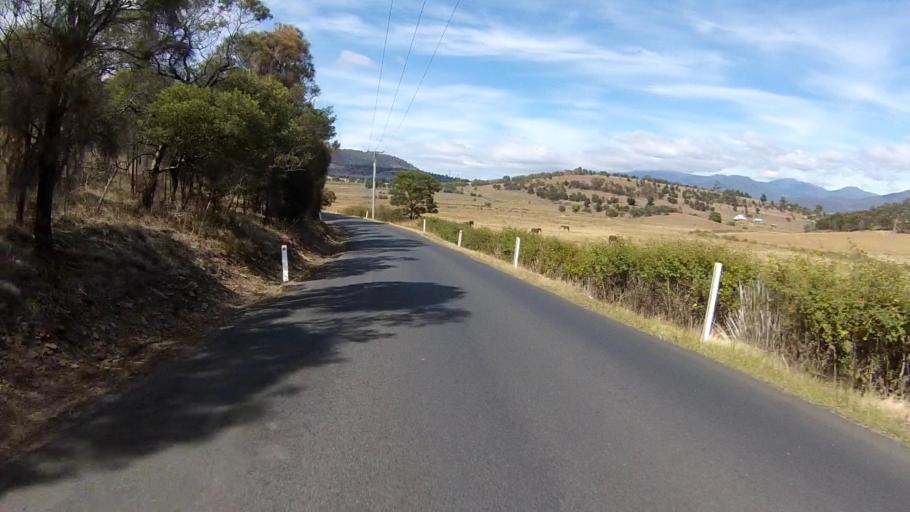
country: AU
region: Tasmania
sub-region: Brighton
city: Old Beach
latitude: -42.7484
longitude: 147.3005
